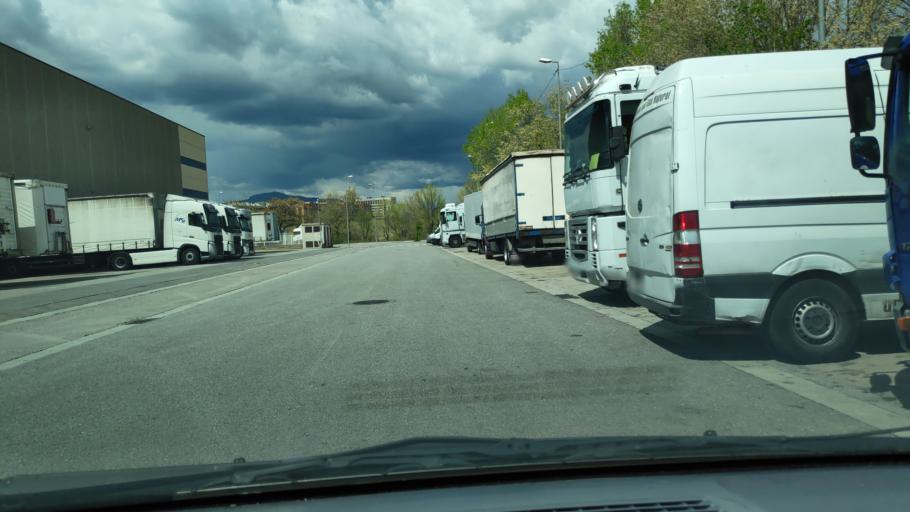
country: ES
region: Catalonia
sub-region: Provincia de Barcelona
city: Polinya
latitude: 41.5437
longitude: 2.1338
